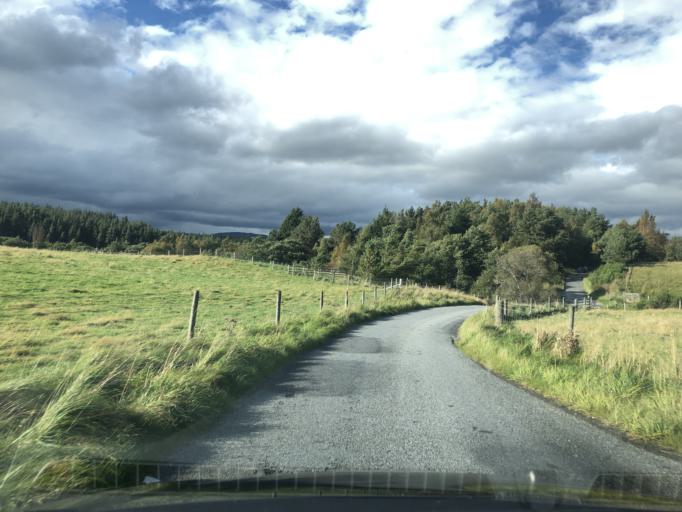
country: GB
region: Scotland
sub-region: Highland
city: Aviemore
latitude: 57.1085
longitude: -3.8893
